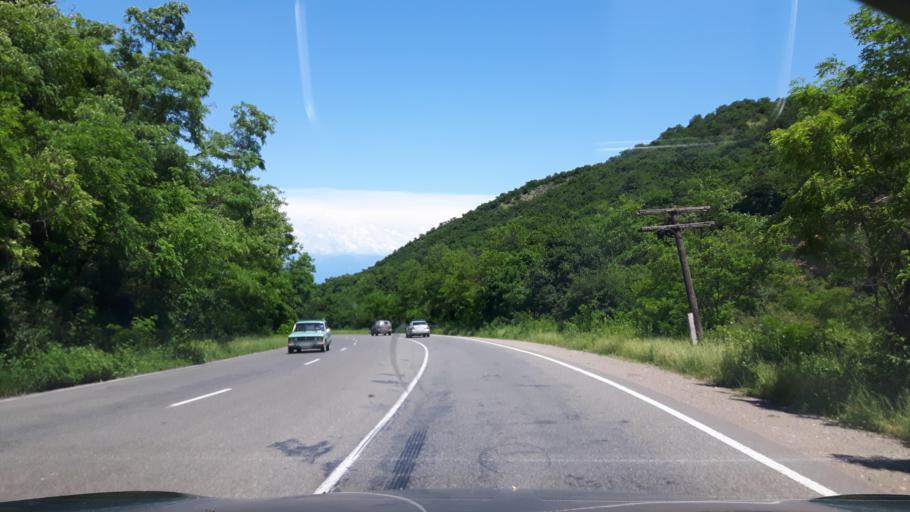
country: GE
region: Kakheti
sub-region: Gurjaani
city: Gurjaani
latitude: 41.6770
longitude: 45.8391
